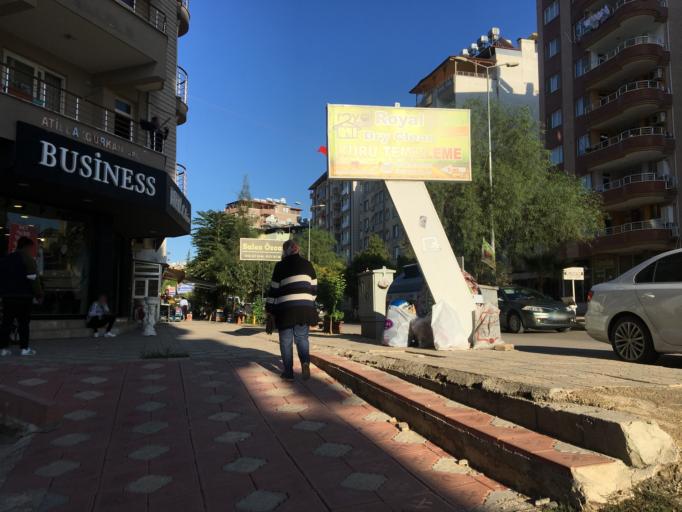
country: TR
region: Hatay
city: Kirikhan
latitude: 36.4930
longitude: 36.3413
